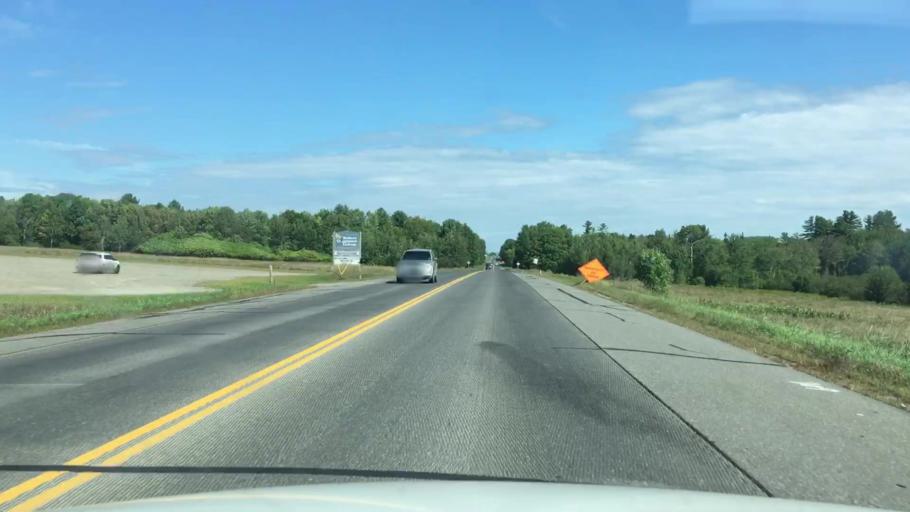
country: US
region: Maine
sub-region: Penobscot County
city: Newport
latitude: 44.8629
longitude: -69.2844
